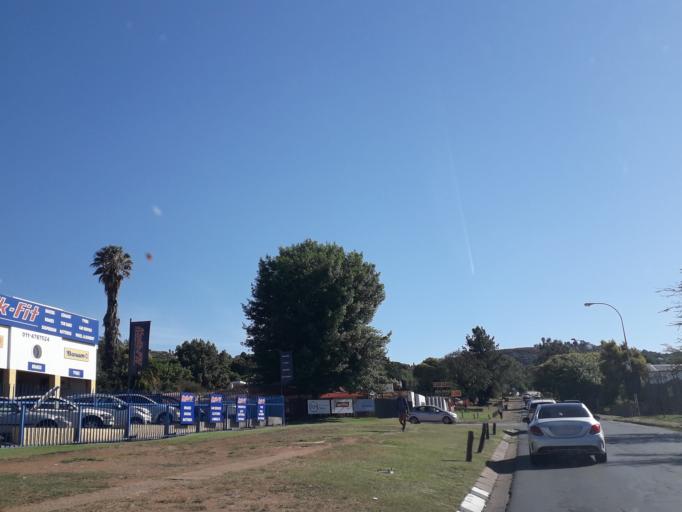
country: ZA
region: Gauteng
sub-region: City of Johannesburg Metropolitan Municipality
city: Roodepoort
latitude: -26.1456
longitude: 27.9528
